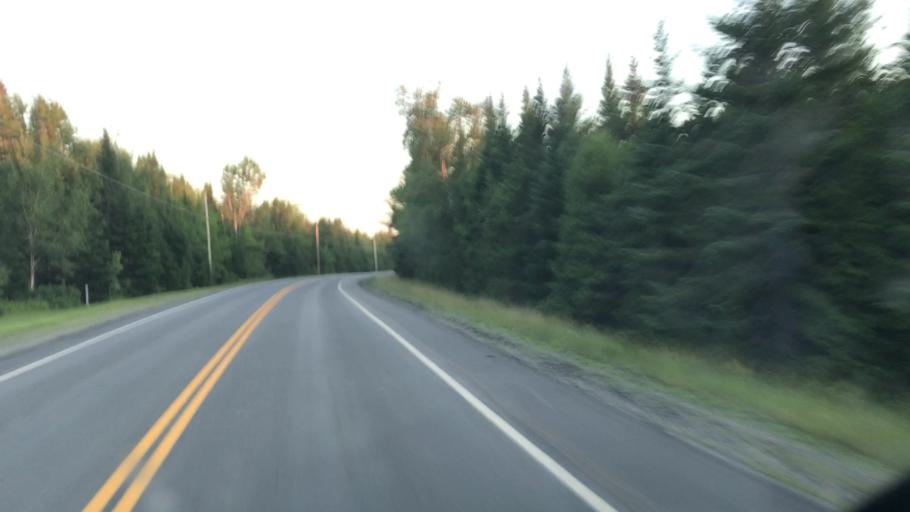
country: US
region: Maine
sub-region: Penobscot County
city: Medway
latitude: 45.5684
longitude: -68.3219
